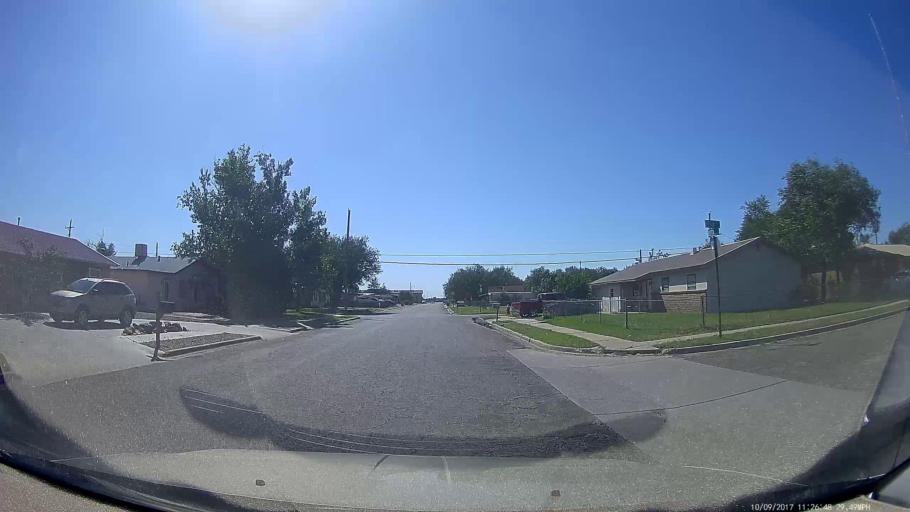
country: US
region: New Mexico
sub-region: Curry County
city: Clovis
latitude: 34.4083
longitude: -103.2272
